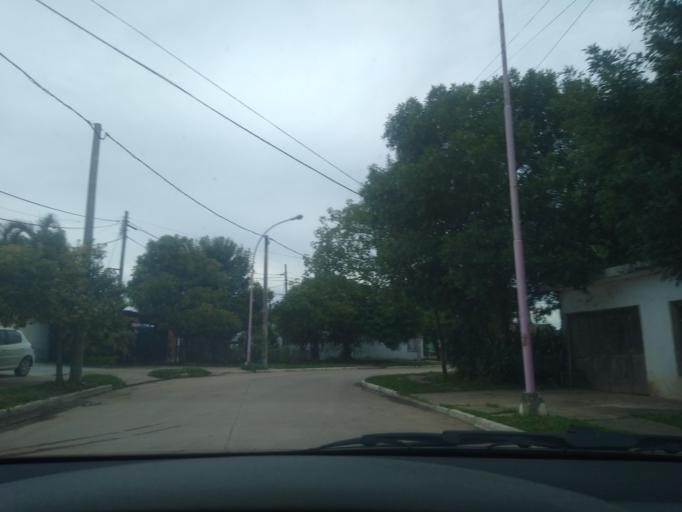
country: AR
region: Chaco
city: Barranqueras
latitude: -27.4647
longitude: -58.9467
